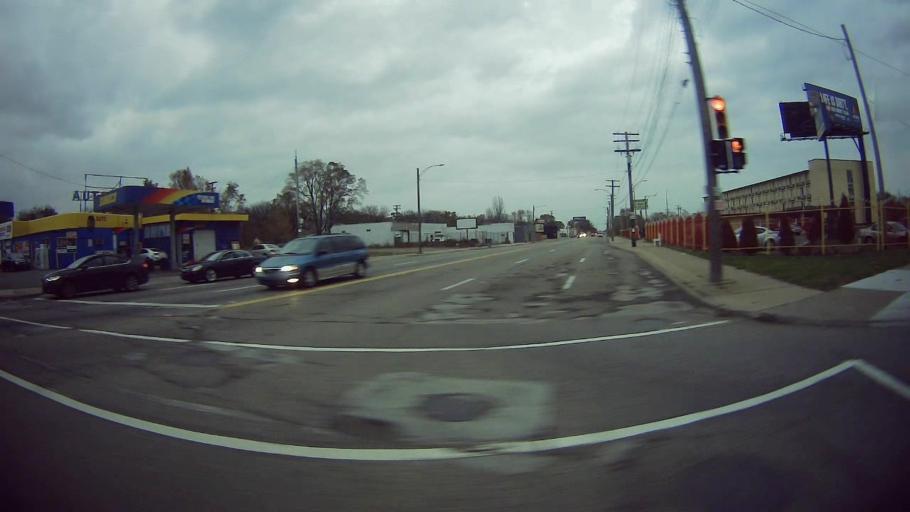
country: US
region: Michigan
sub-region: Wayne County
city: Grosse Pointe Park
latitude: 42.3973
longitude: -82.9894
